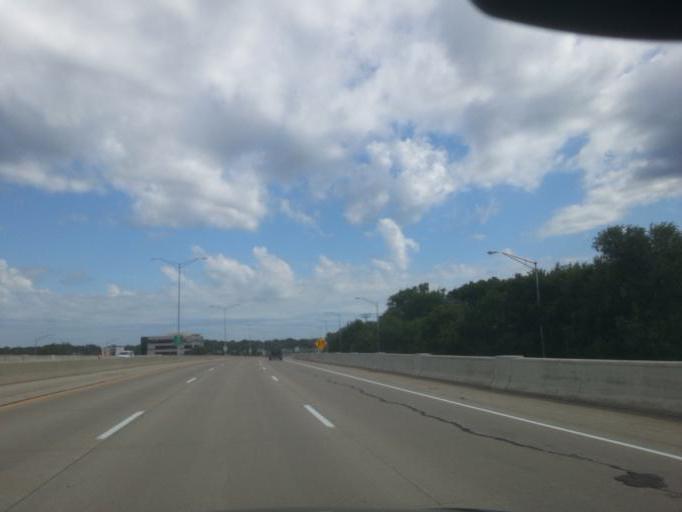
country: US
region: Wisconsin
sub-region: Dane County
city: Monona
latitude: 43.0992
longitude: -89.3165
